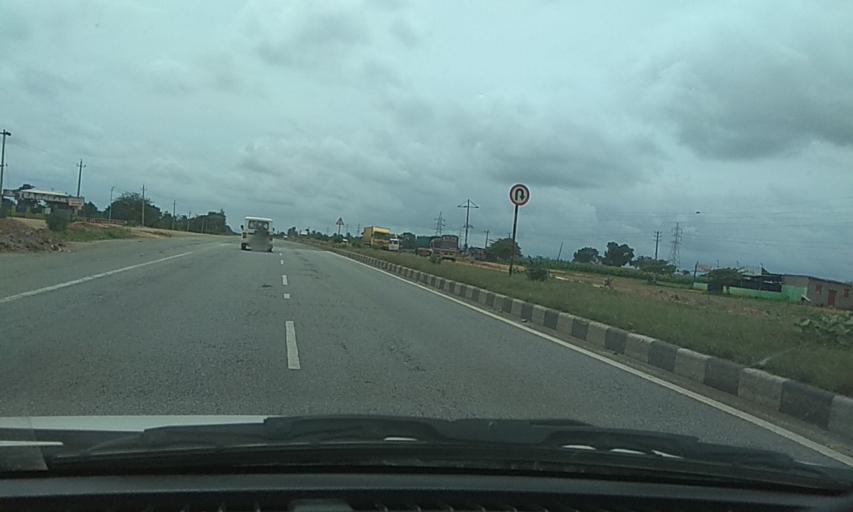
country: IN
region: Karnataka
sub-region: Davanagere
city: Mayakonda
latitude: 14.3308
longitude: 76.2209
